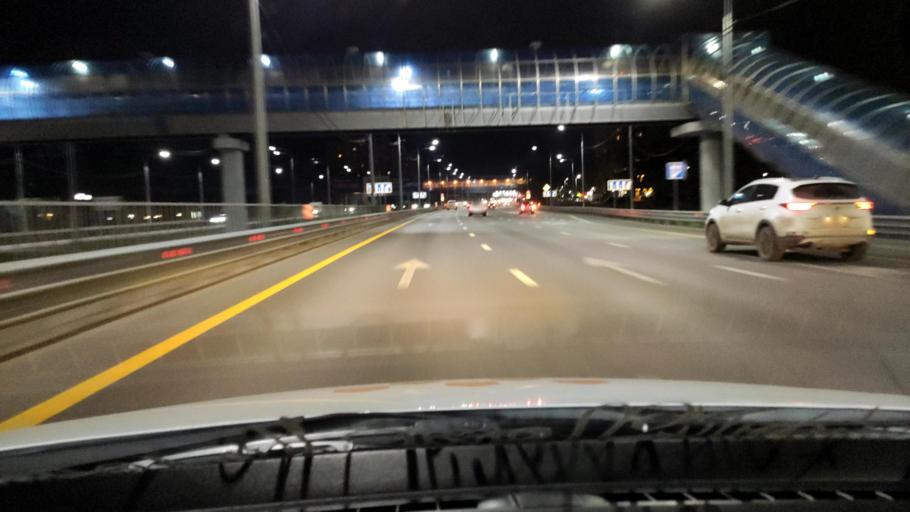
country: RU
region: Voronezj
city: Podgornoye
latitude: 51.7296
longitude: 39.1746
